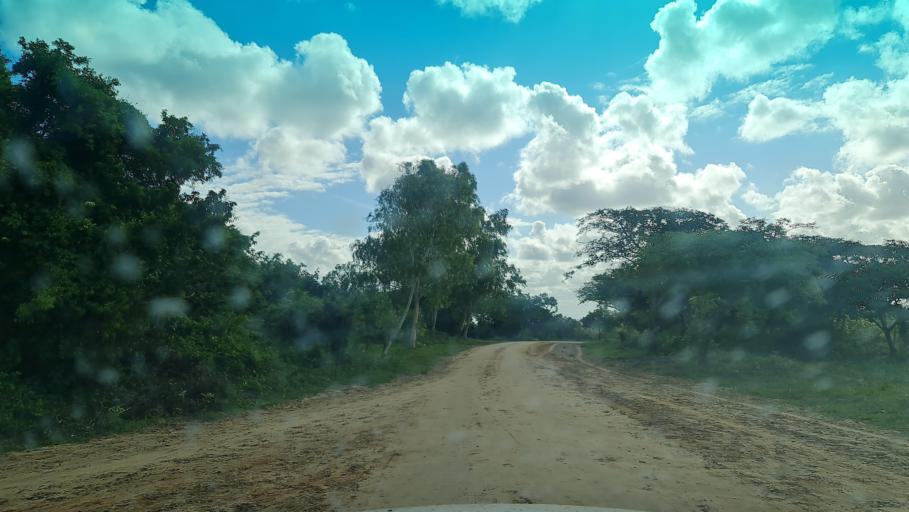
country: MZ
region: Maputo
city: Manhica
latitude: -25.4372
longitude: 32.8820
